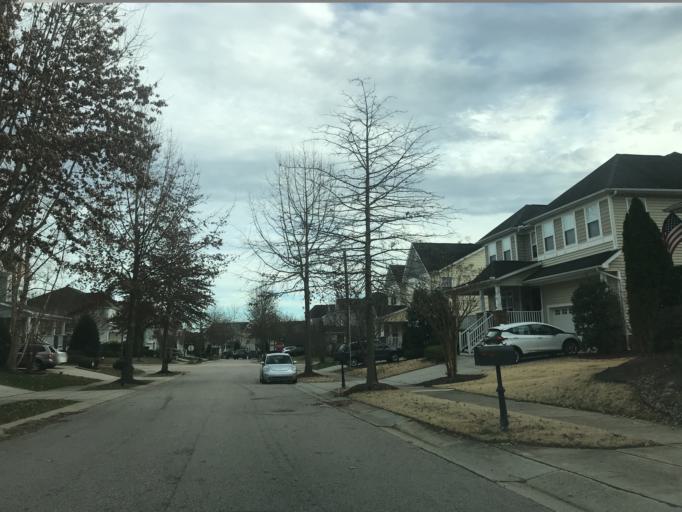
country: US
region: North Carolina
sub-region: Wake County
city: Wake Forest
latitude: 35.9254
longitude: -78.5638
